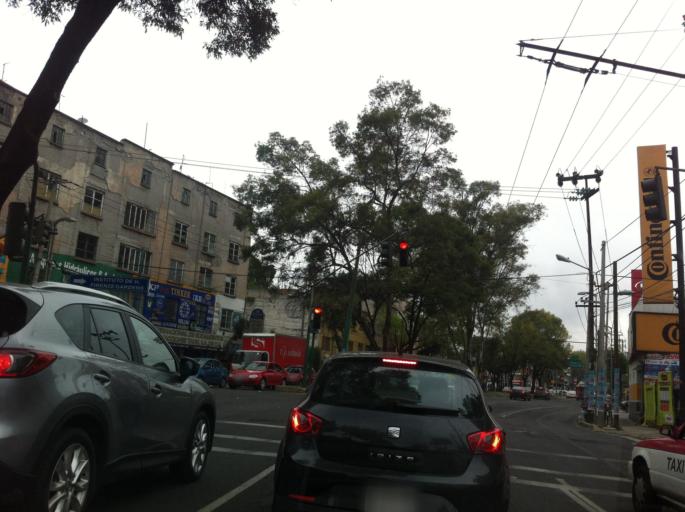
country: MX
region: Mexico City
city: Miguel Hidalgo
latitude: 19.4550
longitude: -99.1811
